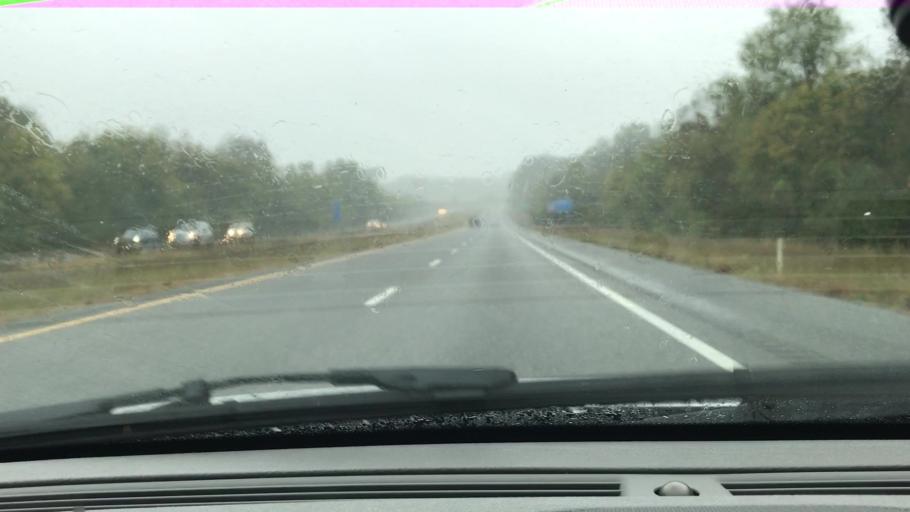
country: US
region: Alabama
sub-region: Limestone County
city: Ardmore
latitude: 35.0012
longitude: -86.8777
